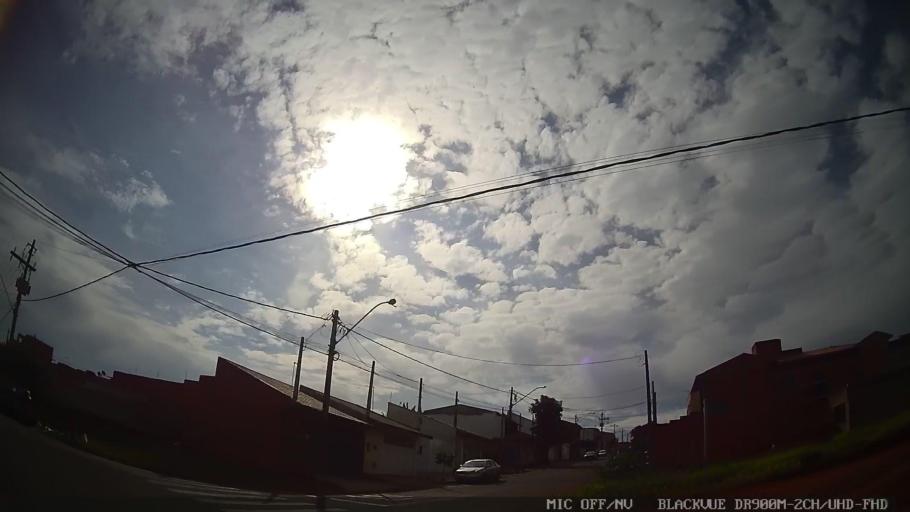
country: BR
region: Sao Paulo
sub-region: Salto
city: Salto
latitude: -23.1835
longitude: -47.2619
